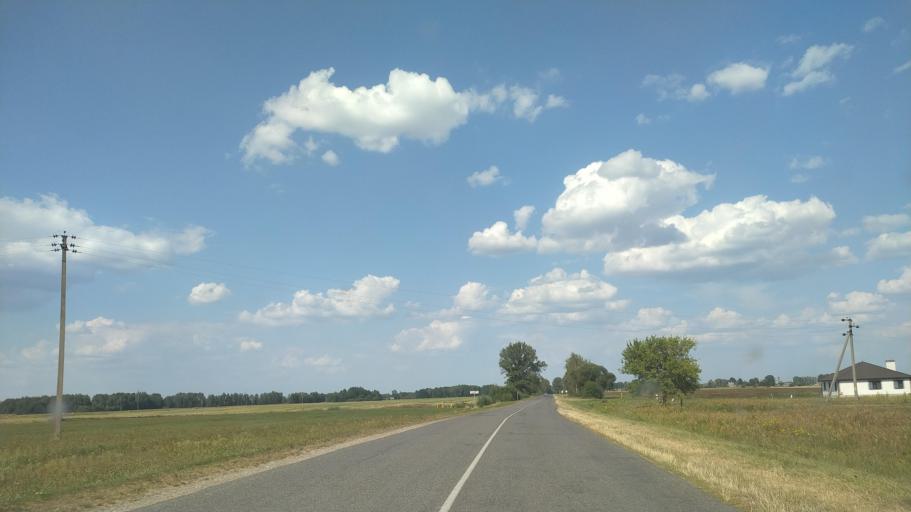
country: BY
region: Brest
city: Drahichyn
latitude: 52.1237
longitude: 25.1165
